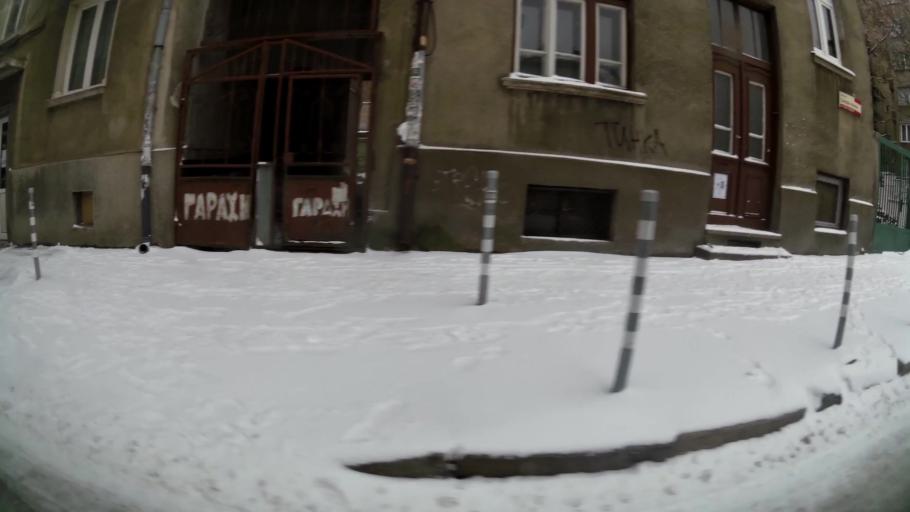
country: BG
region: Sofia-Capital
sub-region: Stolichna Obshtina
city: Sofia
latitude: 42.7001
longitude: 23.3351
